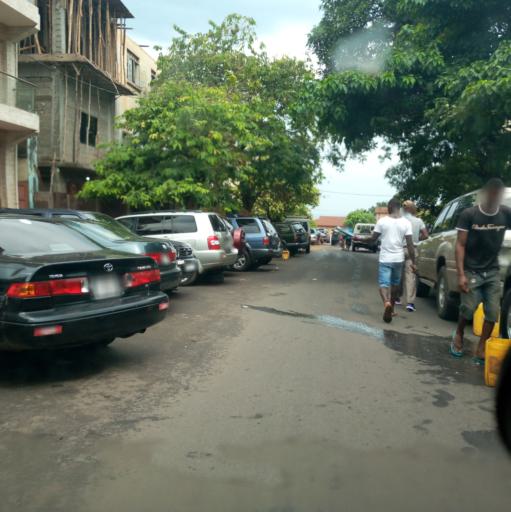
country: SL
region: Western Area
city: Freetown
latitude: 8.4882
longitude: -13.2357
